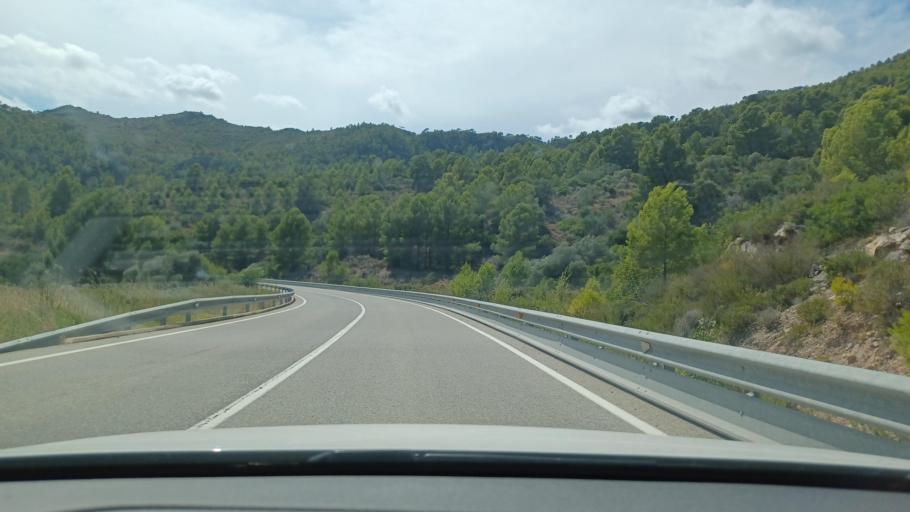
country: ES
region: Catalonia
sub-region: Provincia de Tarragona
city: Tivenys
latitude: 40.9449
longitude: 0.4598
